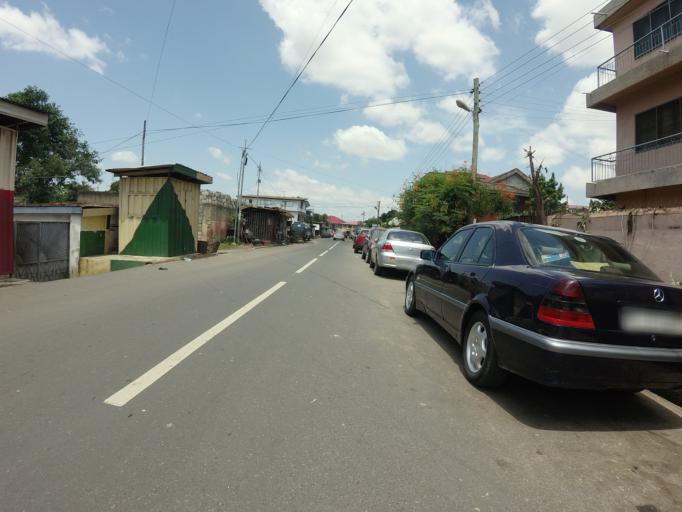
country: GH
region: Greater Accra
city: Accra
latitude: 5.5774
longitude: -0.2033
